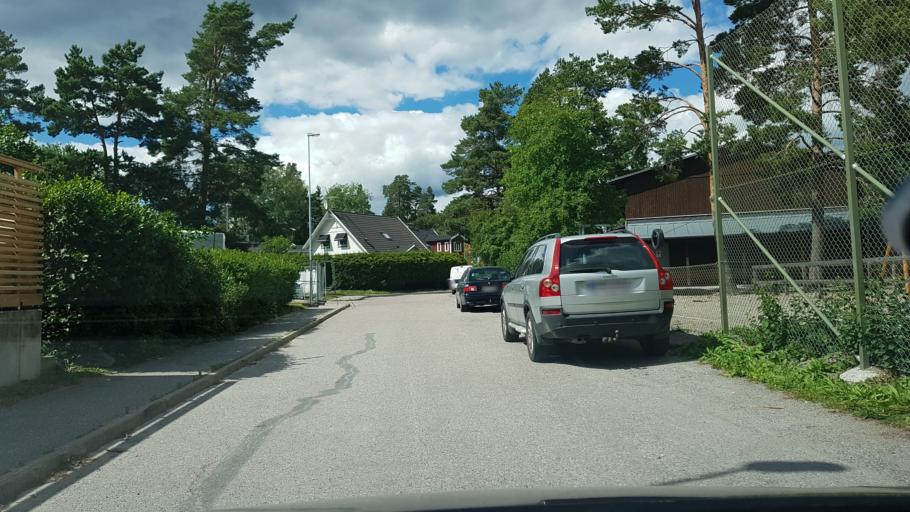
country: SE
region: Stockholm
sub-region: Upplands-Bro Kommun
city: Kungsaengen
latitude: 59.4789
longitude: 17.8052
